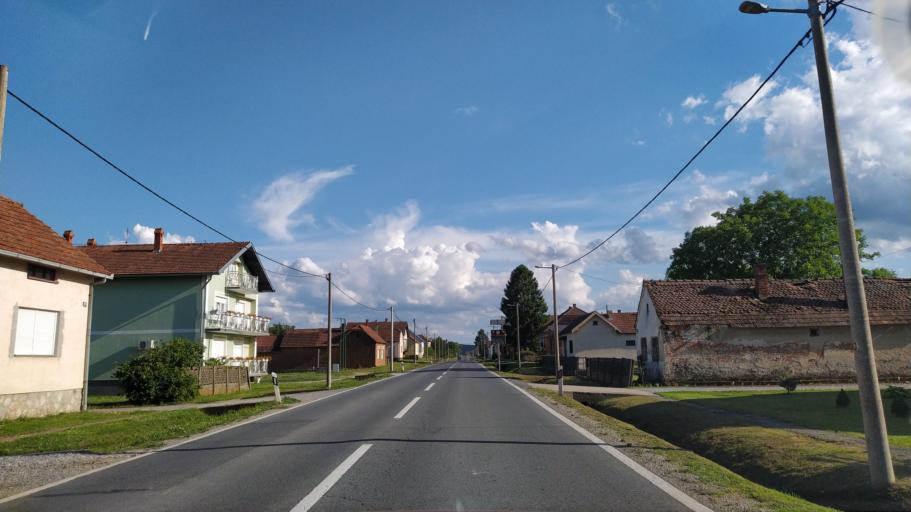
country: HR
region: Virovitick-Podravska
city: Spisic-Bukovica
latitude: 45.8848
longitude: 17.2892
